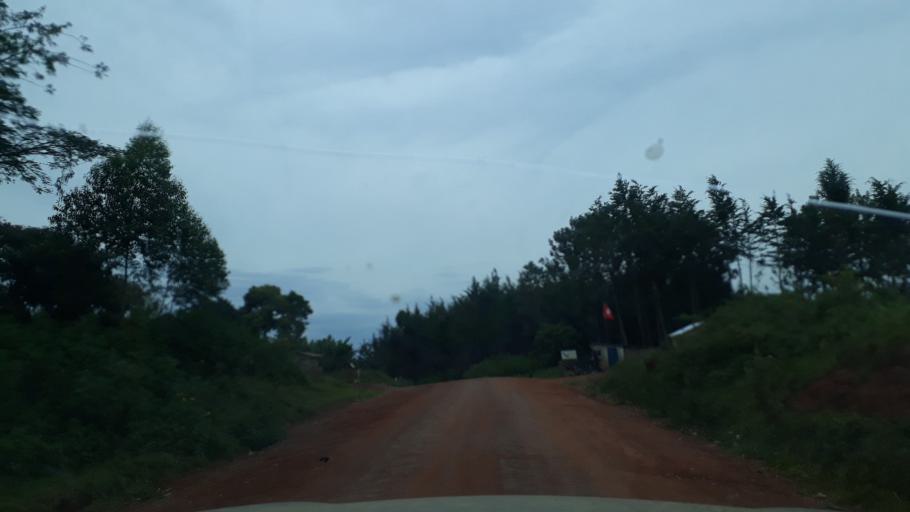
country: UG
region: Northern Region
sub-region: Zombo District
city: Paidha
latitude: 2.1941
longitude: 30.7281
